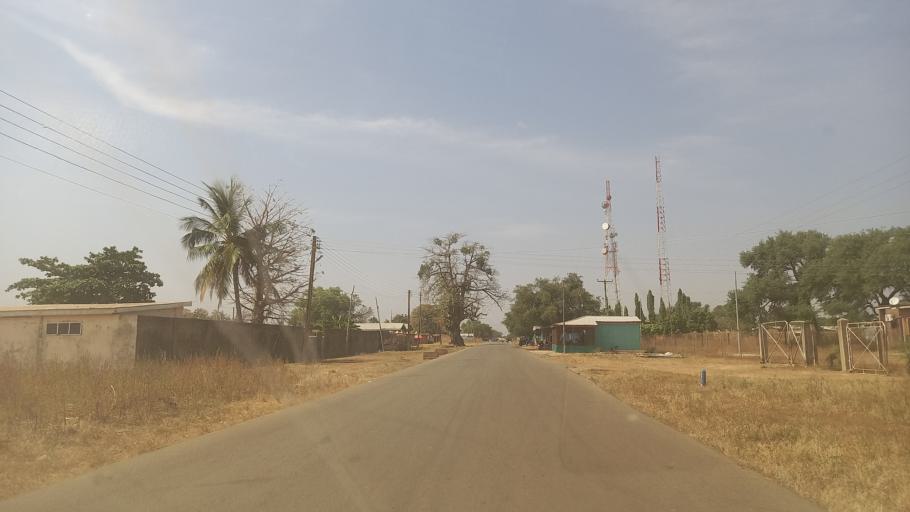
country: GH
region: Upper East
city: Navrongo
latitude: 10.8828
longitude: -1.0809
